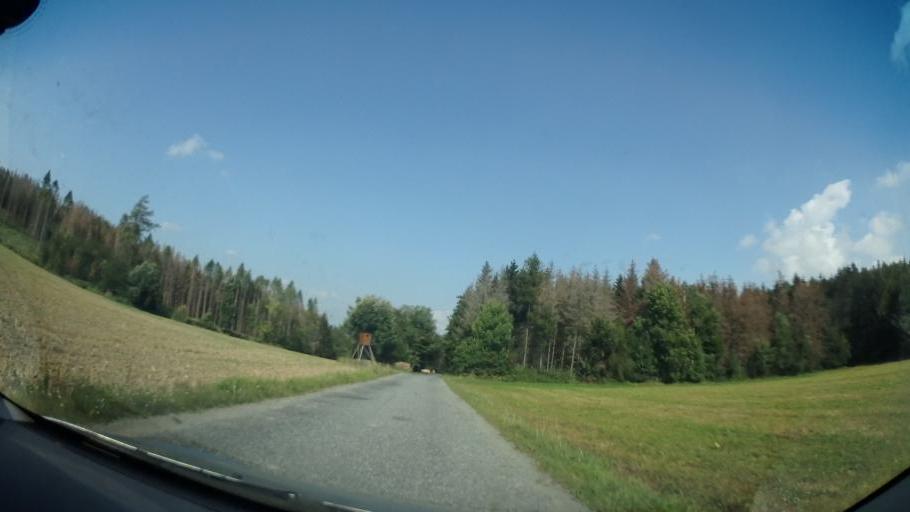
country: CZ
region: South Moravian
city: Olesnice
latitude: 49.5547
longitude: 16.3513
